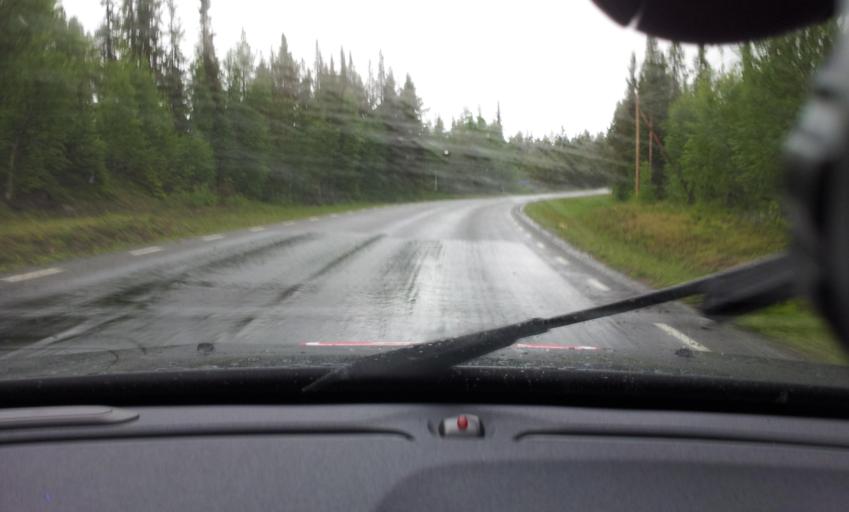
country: SE
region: Jaemtland
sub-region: Are Kommun
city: Are
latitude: 63.2106
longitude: 13.1601
